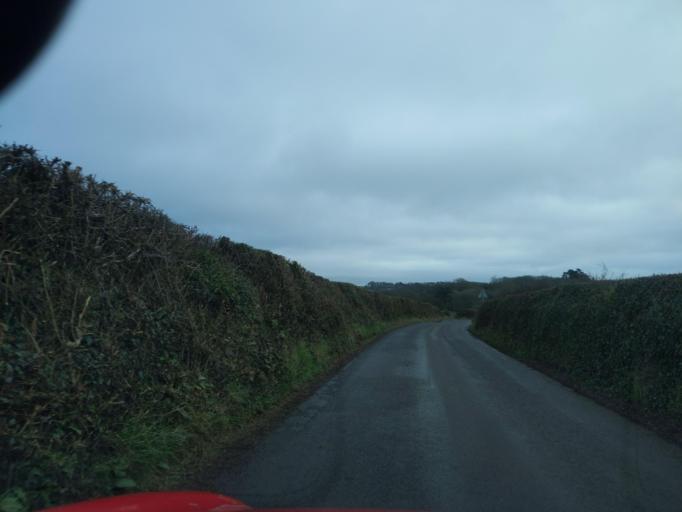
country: GB
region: England
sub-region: Devon
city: Wembury
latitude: 50.3294
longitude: -4.0940
